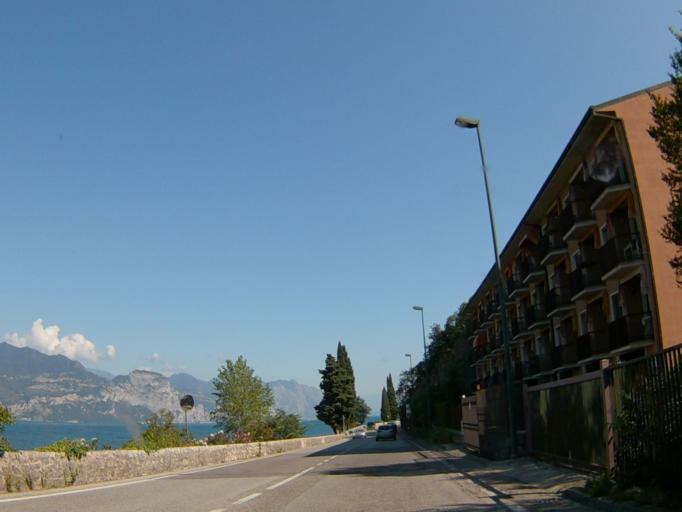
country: IT
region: Veneto
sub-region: Provincia di Verona
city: San Zeno di Montagna
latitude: 45.6667
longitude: 10.7317
